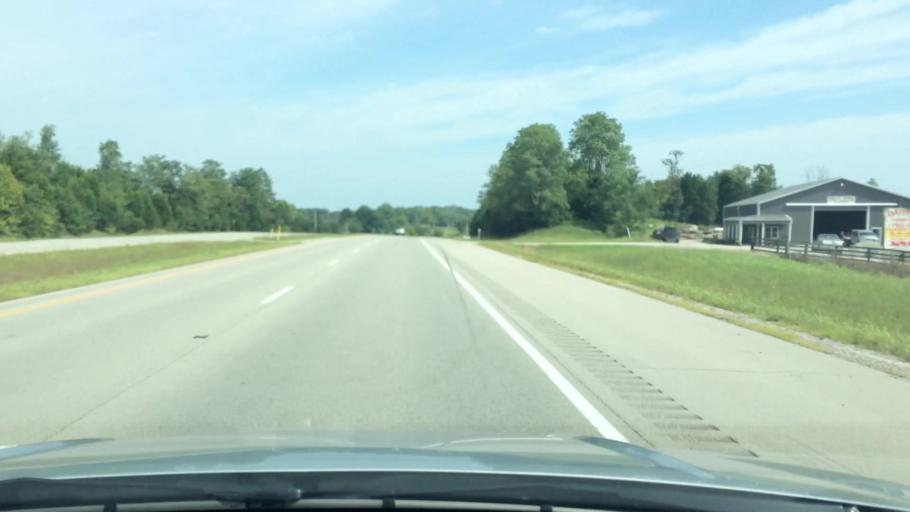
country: US
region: Kentucky
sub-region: Franklin County
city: Frankfort
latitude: 38.1270
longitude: -84.9148
